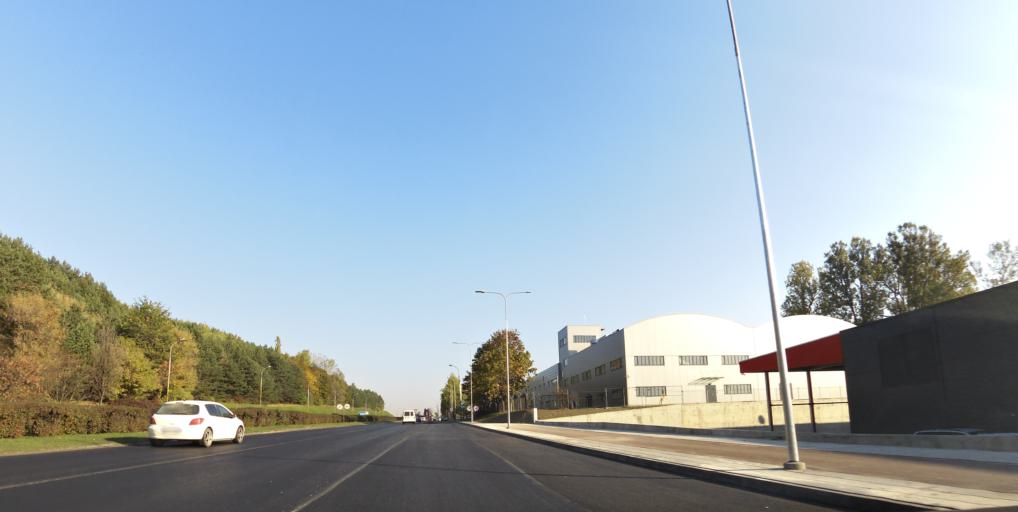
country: LT
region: Vilnius County
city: Seskine
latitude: 54.7062
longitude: 25.2670
